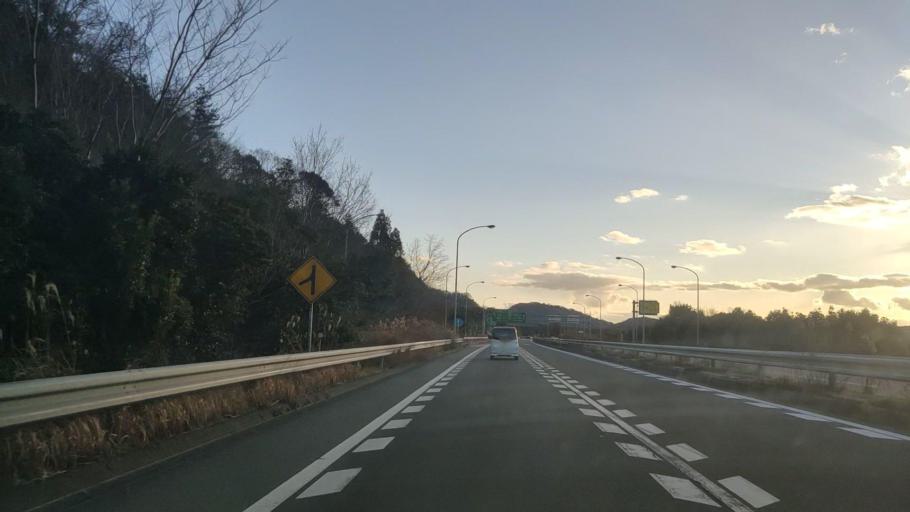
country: JP
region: Hyogo
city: Tatsunocho-tominaga
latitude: 34.8507
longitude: 134.6046
